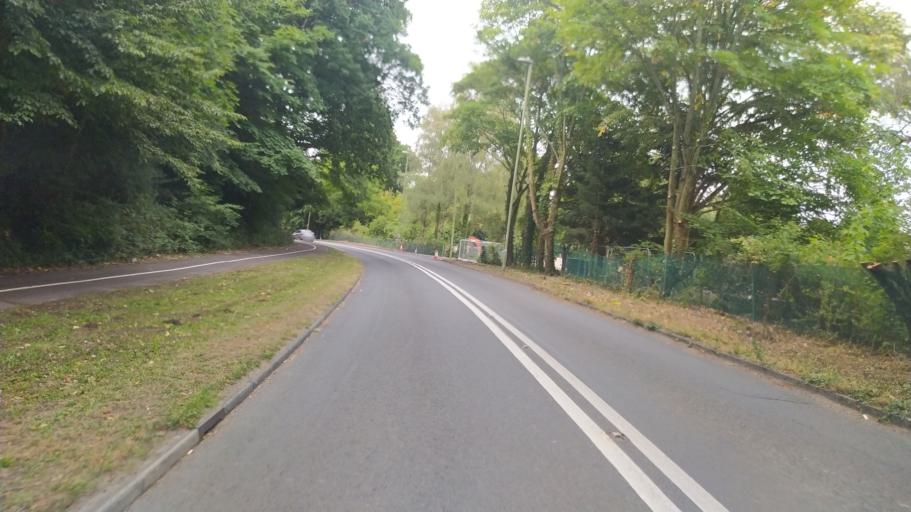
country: GB
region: England
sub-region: Hampshire
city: Havant
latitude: 50.8771
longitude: -0.9730
